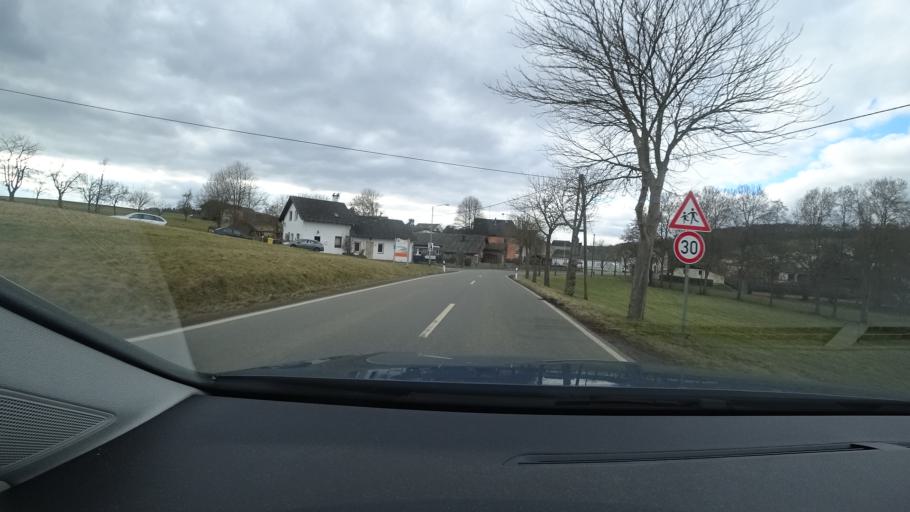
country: DE
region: Rheinland-Pfalz
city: Geisig
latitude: 50.2530
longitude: 7.7937
